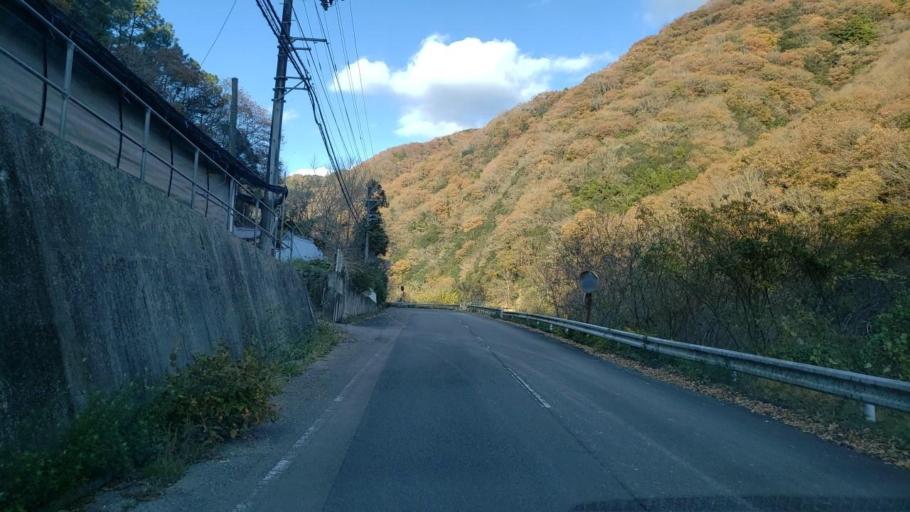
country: JP
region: Tokushima
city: Wakimachi
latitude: 34.0844
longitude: 134.0729
